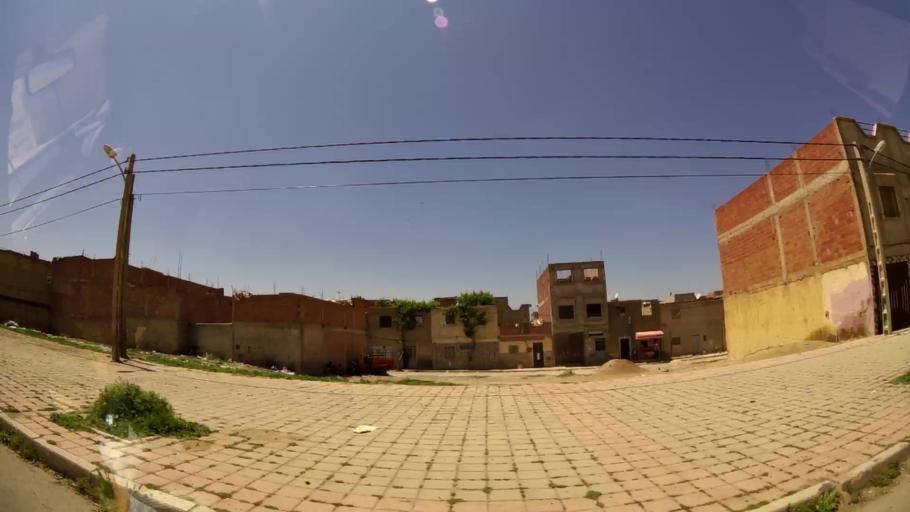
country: MA
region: Oriental
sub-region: Oujda-Angad
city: Oujda
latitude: 34.6939
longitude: -1.9467
